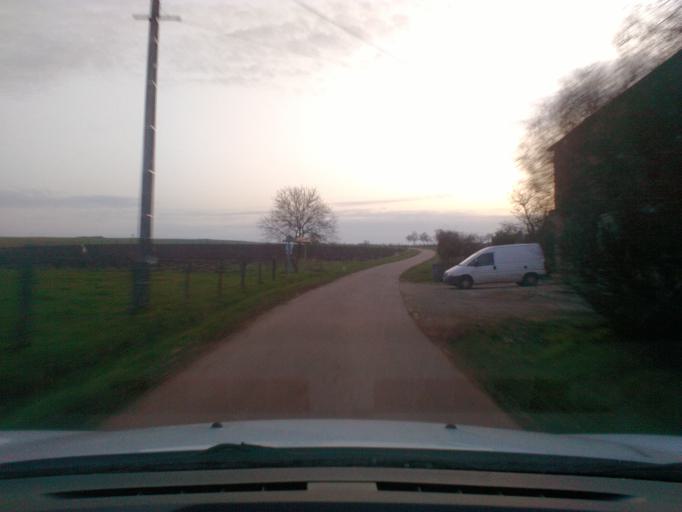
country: FR
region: Lorraine
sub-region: Departement des Vosges
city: Mirecourt
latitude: 48.3741
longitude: 6.1863
